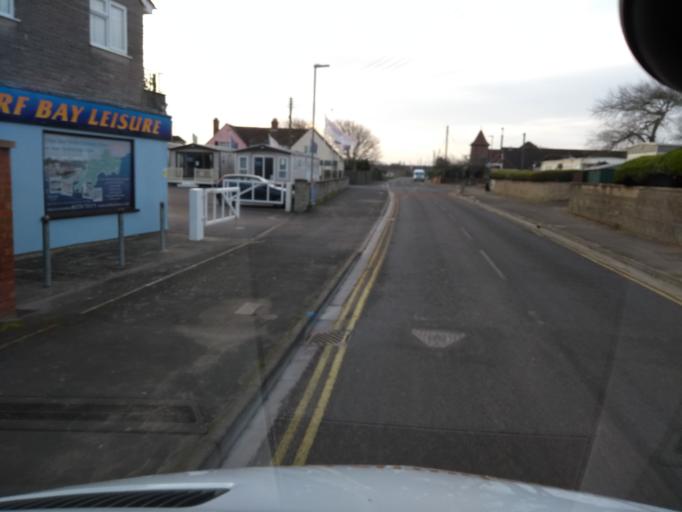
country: GB
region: England
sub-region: North Somerset
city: Weston-super-Mare
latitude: 51.3010
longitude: -3.0101
